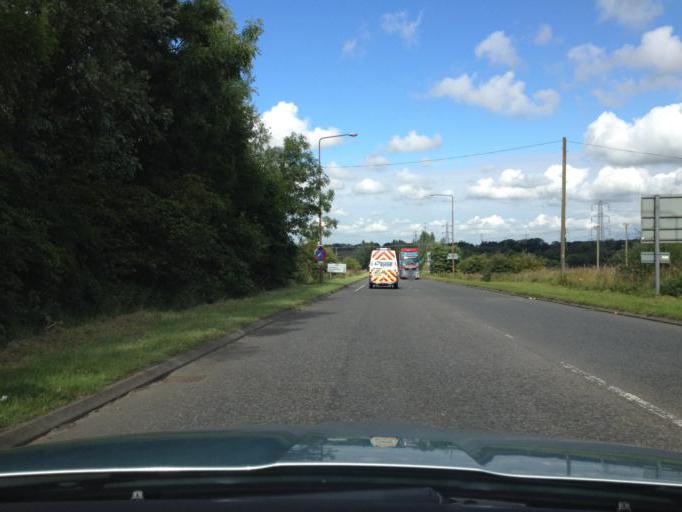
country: GB
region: Scotland
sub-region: West Lothian
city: Whitburn
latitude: 55.8805
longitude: -3.6621
